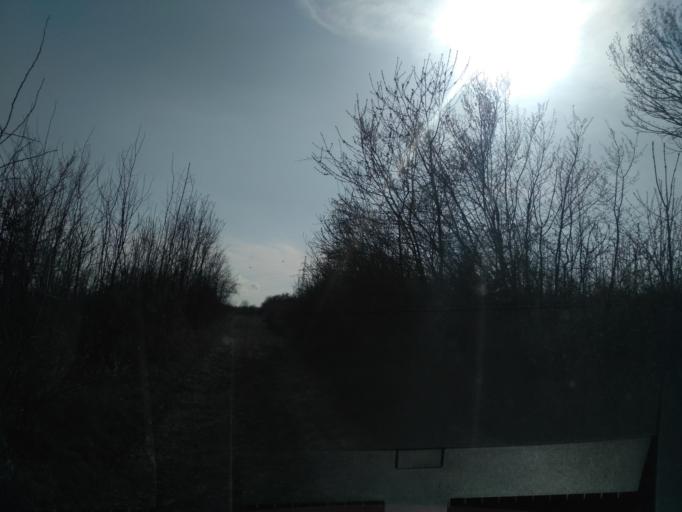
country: SK
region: Kosicky
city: Kosice
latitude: 48.6889
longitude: 21.1862
